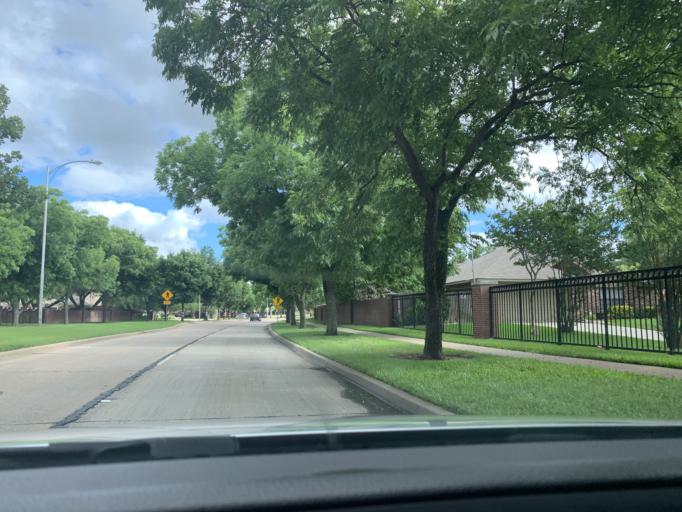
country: US
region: Texas
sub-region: Dallas County
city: Grand Prairie
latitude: 32.6661
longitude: -97.0022
